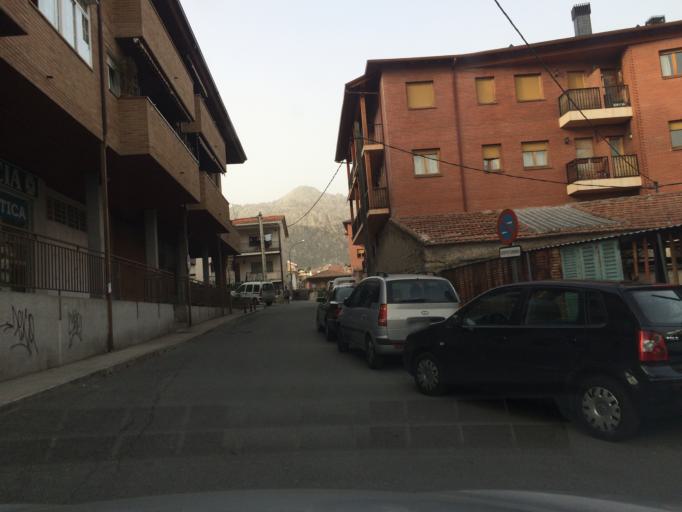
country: ES
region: Madrid
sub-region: Provincia de Madrid
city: Manzanares el Real
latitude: 40.7261
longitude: -3.8666
